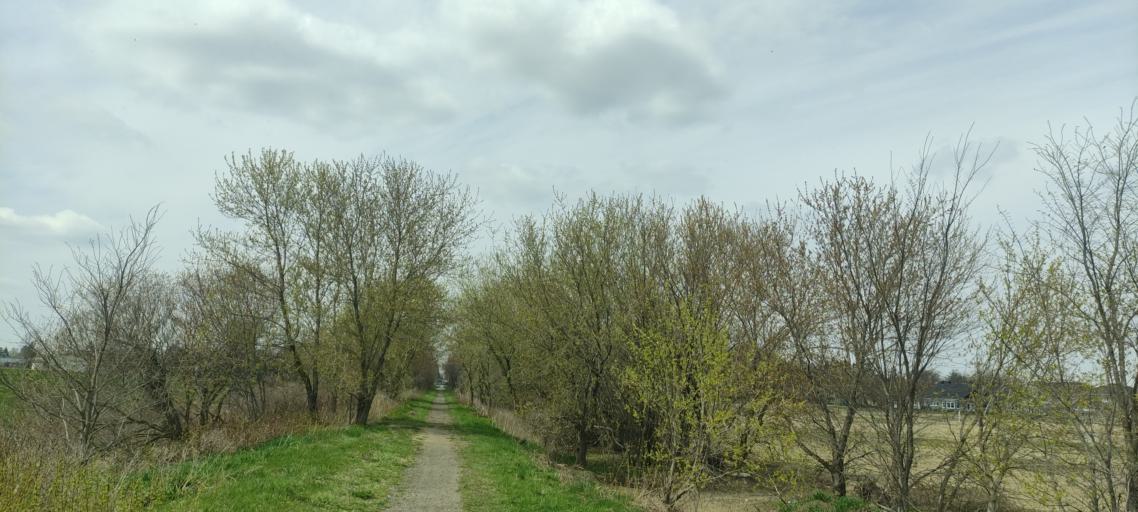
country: CA
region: Ontario
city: Stratford
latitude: 43.3186
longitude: -80.8268
